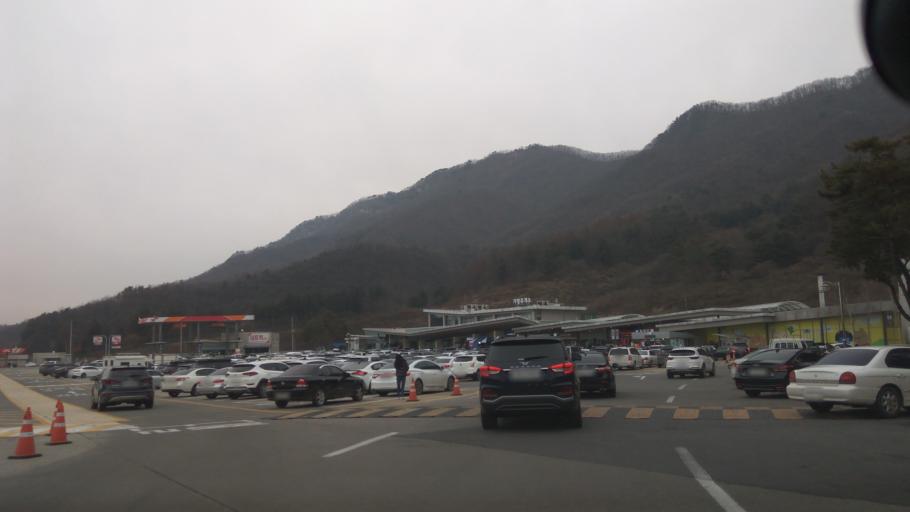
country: KR
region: Gyeonggi-do
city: Cheongpyeong
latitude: 37.7012
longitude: 127.5453
